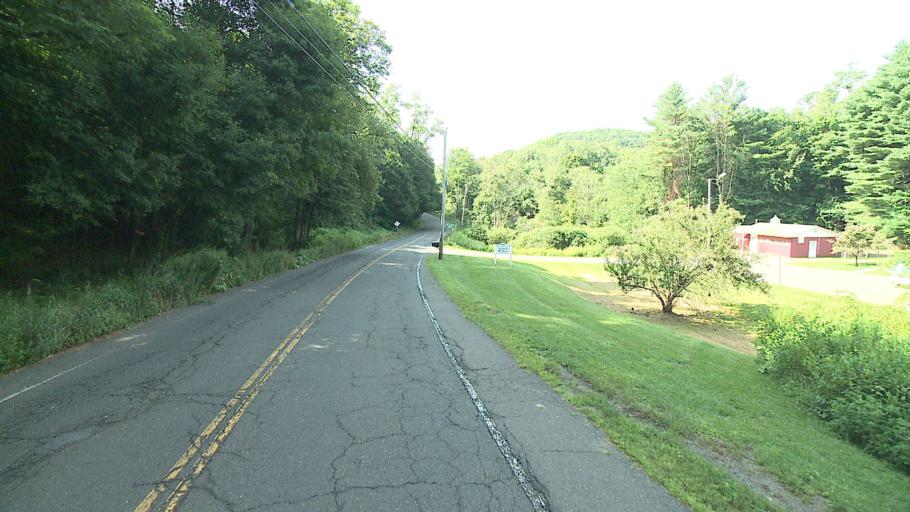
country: US
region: New York
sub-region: Putnam County
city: Putnam Lake
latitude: 41.4979
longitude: -73.5294
